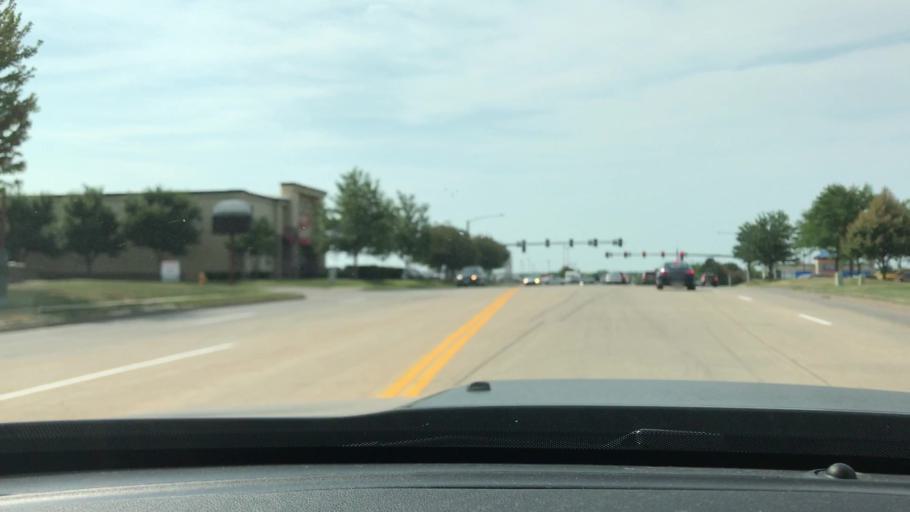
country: US
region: Iowa
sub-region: Scott County
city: Bettendorf
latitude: 41.5763
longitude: -90.5287
